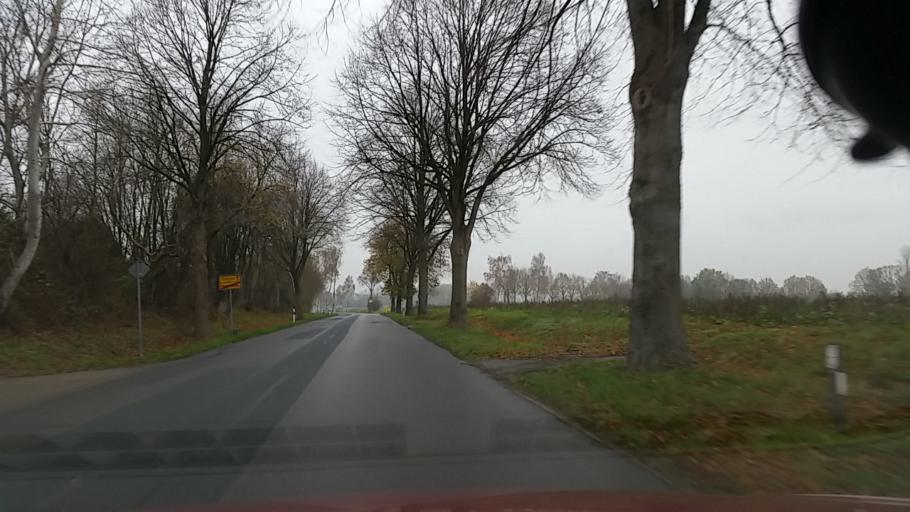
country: DE
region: Lower Saxony
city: Hankensbuttel
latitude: 52.7369
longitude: 10.6046
